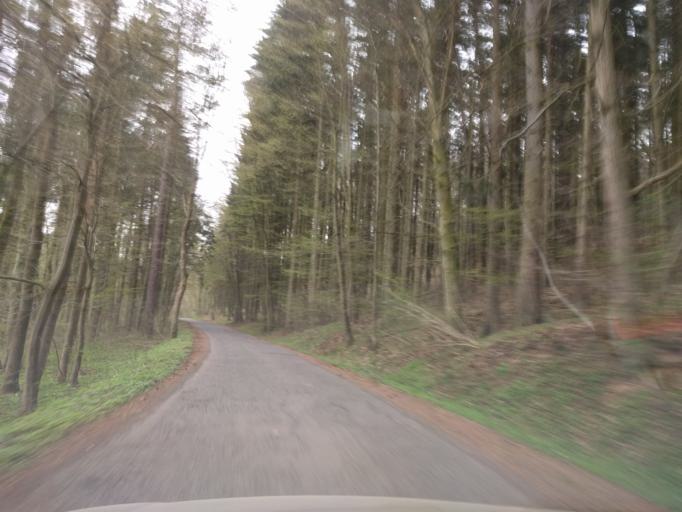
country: CZ
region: Central Bohemia
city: Kostelec nad Cernymi Lesy
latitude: 50.0236
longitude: 14.8141
